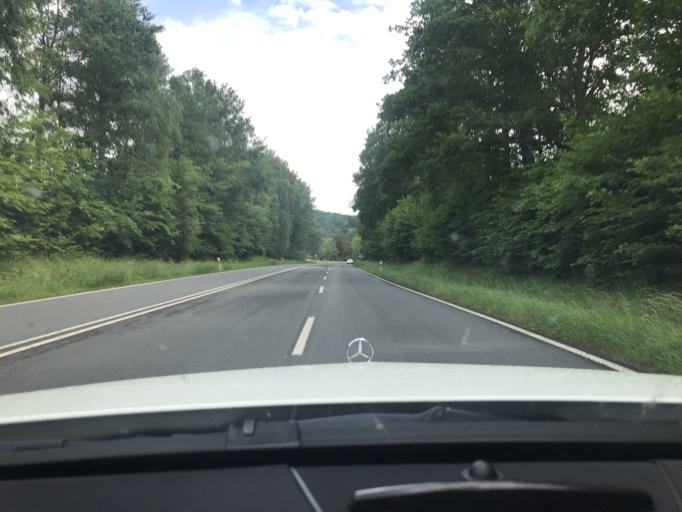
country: DE
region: Hesse
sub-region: Regierungsbezirk Kassel
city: Sontra
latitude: 51.0685
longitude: 9.9233
